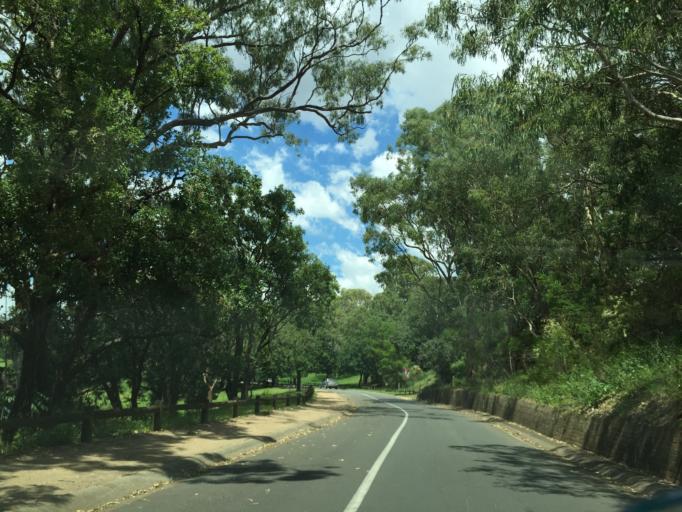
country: AU
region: New South Wales
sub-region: Parramatta
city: City of Parramatta
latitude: -33.8085
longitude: 150.9958
